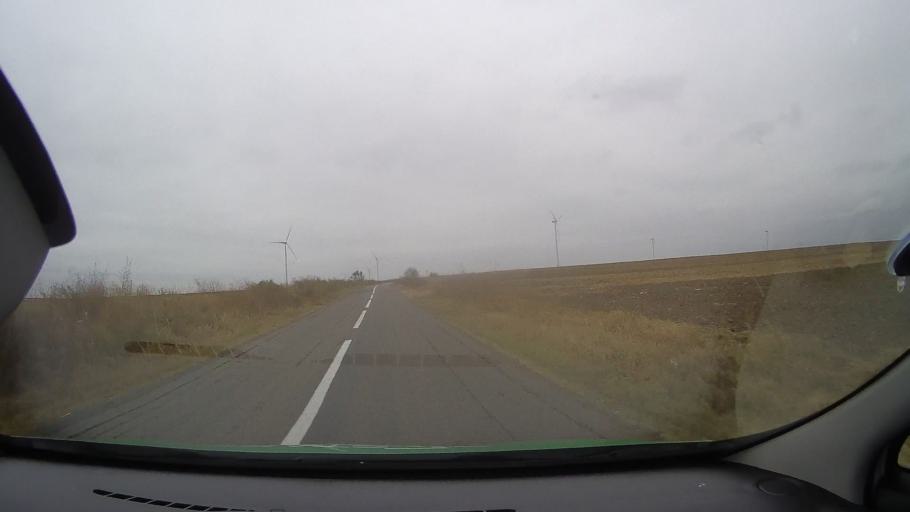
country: RO
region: Constanta
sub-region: Comuna Pantelimon
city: Pantelimon
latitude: 44.5015
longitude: 28.3536
